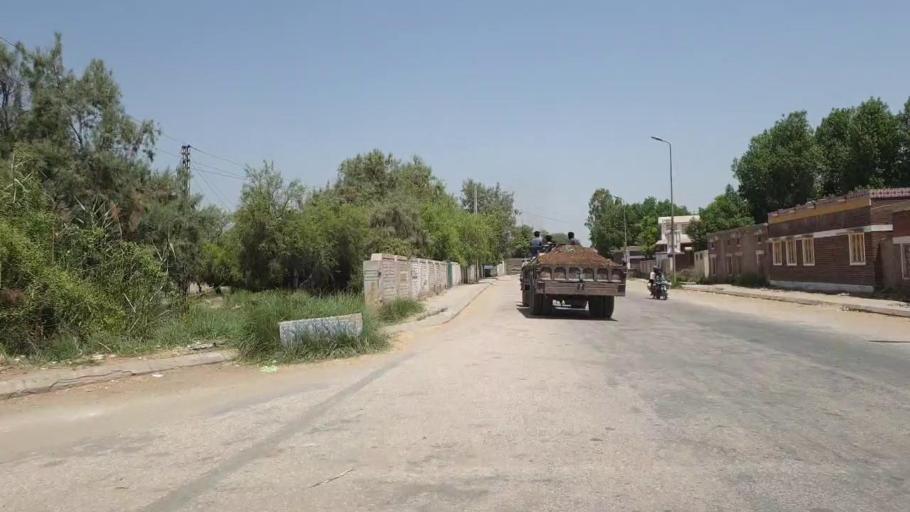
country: PK
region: Sindh
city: Adilpur
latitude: 27.9403
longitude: 69.3183
